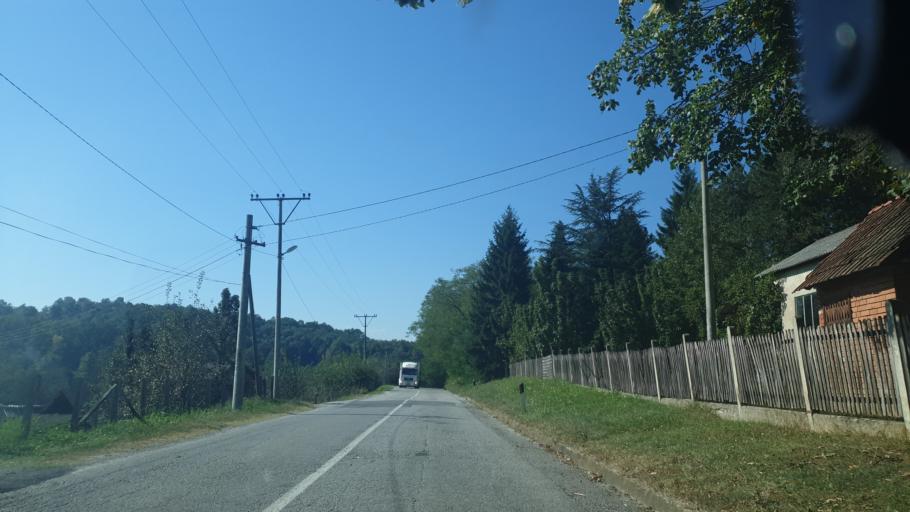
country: RS
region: Central Serbia
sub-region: Kolubarski Okrug
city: Lajkovac
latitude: 44.3240
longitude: 20.1938
